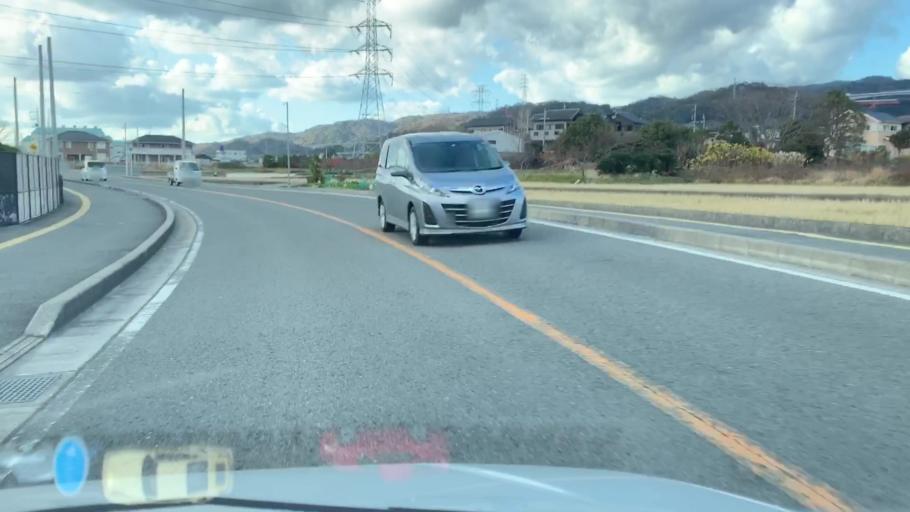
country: JP
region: Wakayama
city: Iwade
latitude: 34.2724
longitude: 135.2808
